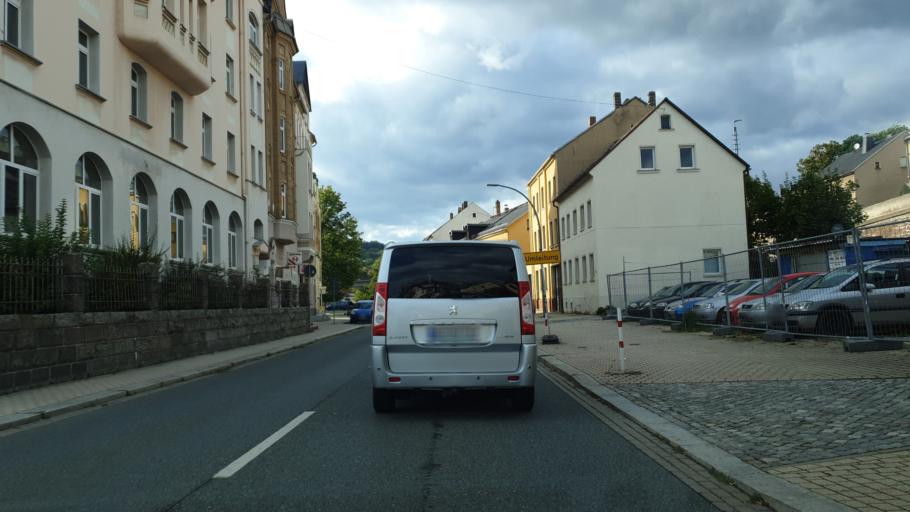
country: DE
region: Saxony
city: Aue
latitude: 50.5893
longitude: 12.7017
